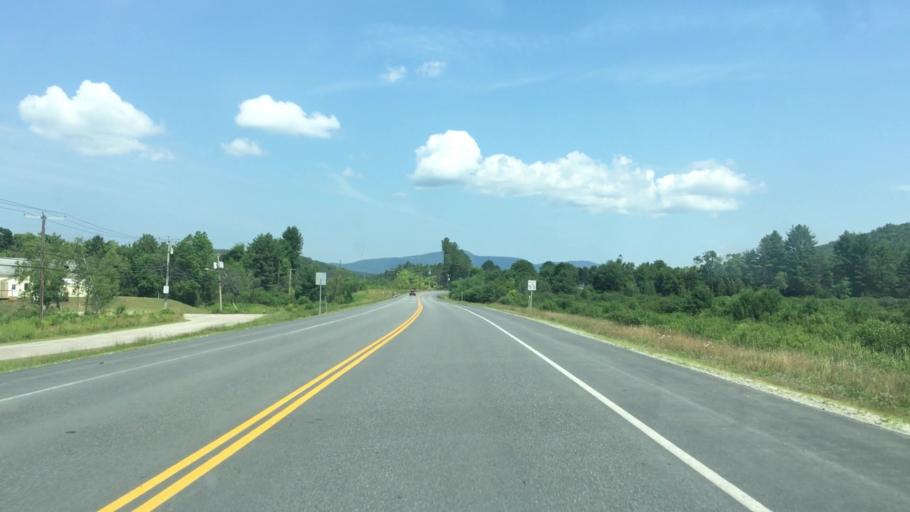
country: US
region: New Hampshire
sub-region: Sullivan County
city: Newport
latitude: 43.3809
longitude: -72.1805
